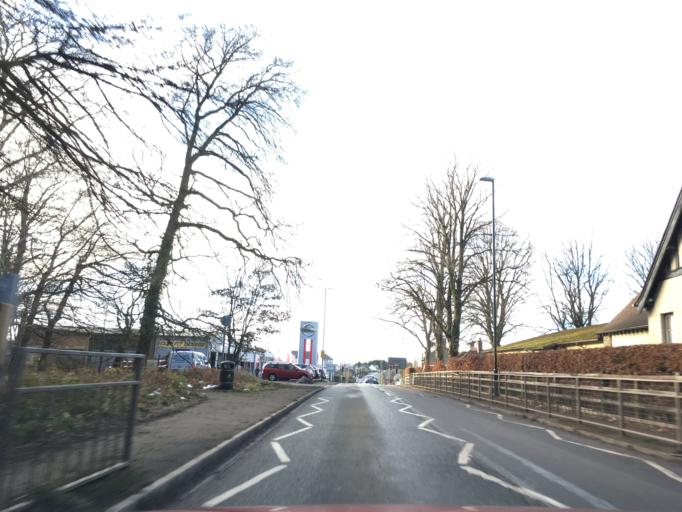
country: GB
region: England
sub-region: Gloucestershire
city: Coleford
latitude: 51.8084
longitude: -2.6086
